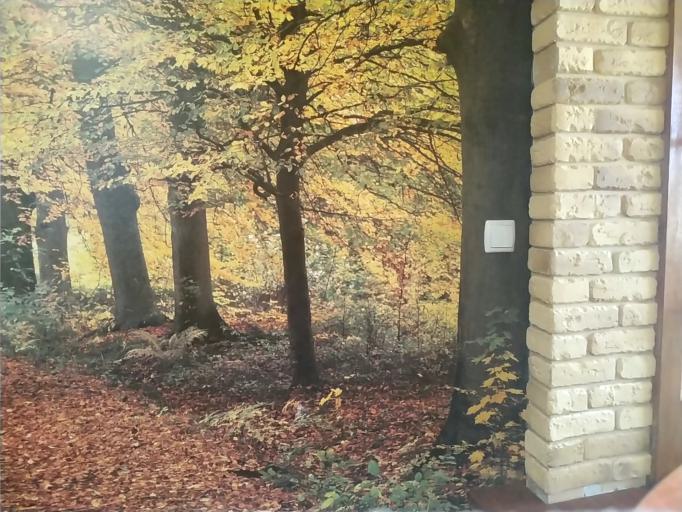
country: RU
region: Tverskaya
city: Vyshniy Volochek
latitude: 57.6842
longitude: 34.5137
